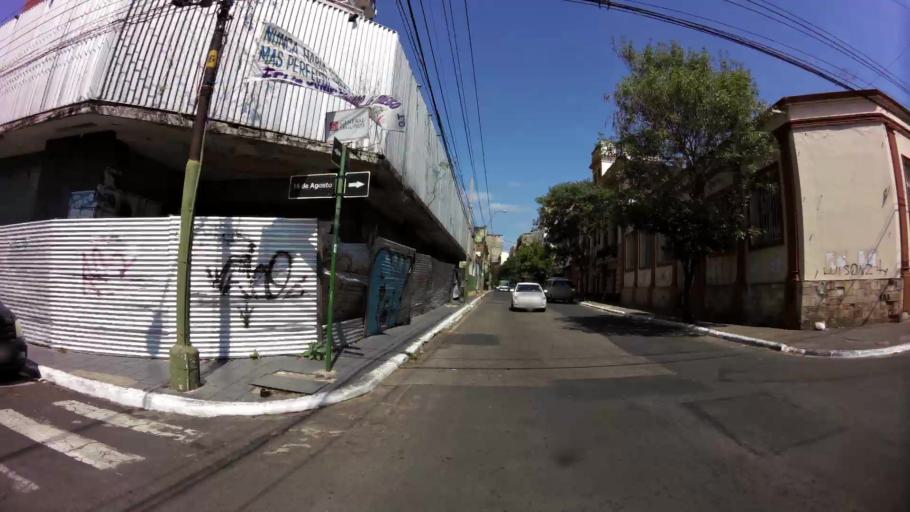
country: PY
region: Asuncion
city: Asuncion
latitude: -25.2798
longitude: -57.6370
